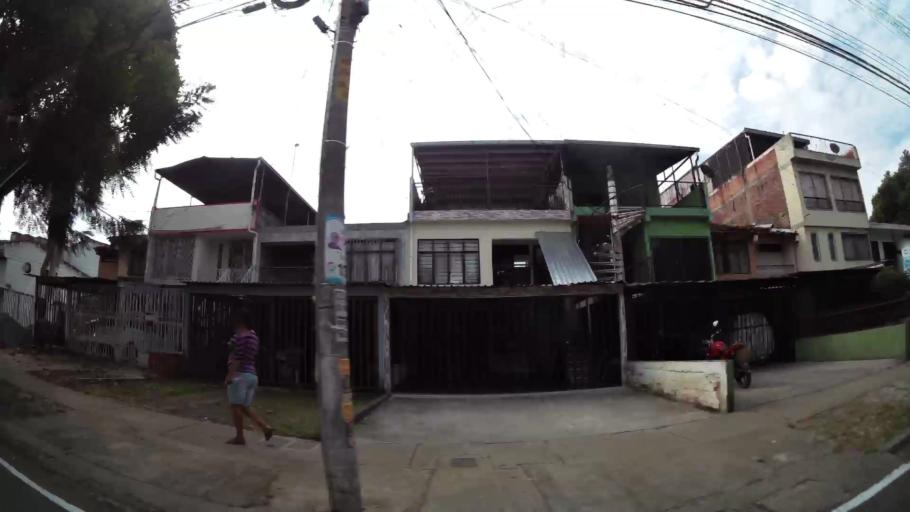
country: CO
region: Valle del Cauca
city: Cali
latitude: 3.4757
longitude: -76.4894
